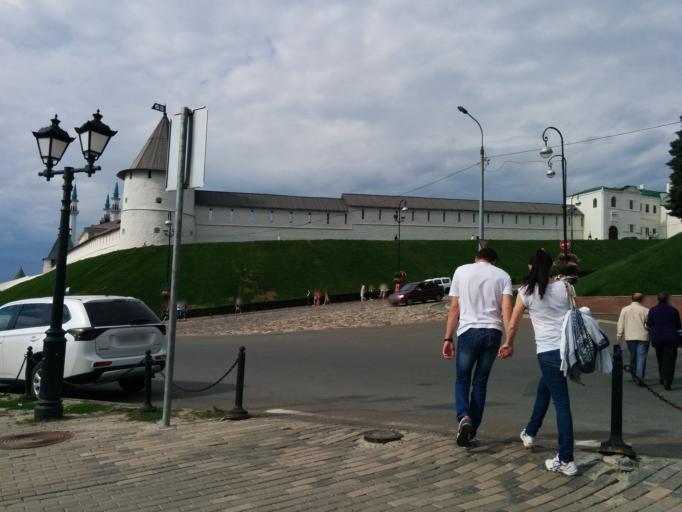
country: RU
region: Tatarstan
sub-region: Gorod Kazan'
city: Kazan
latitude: 55.7954
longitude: 49.1068
